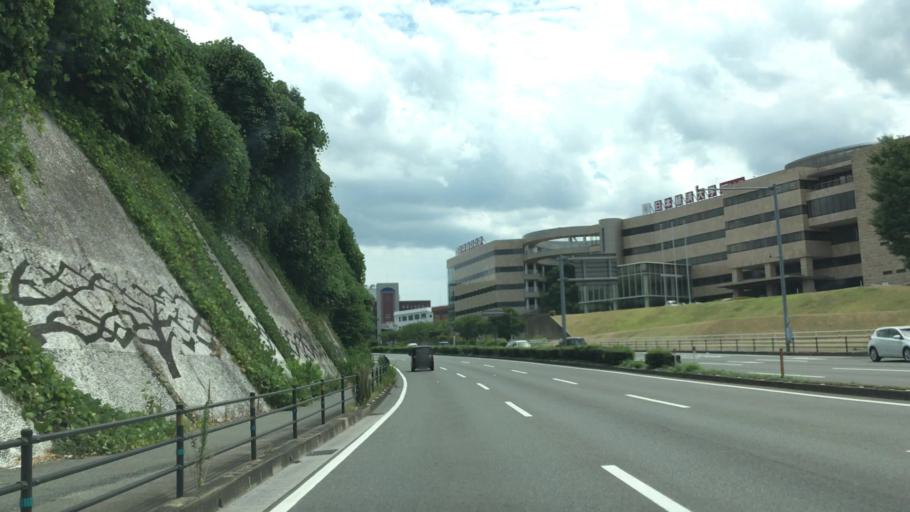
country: JP
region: Fukuoka
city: Dazaifu
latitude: 33.5080
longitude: 130.5244
